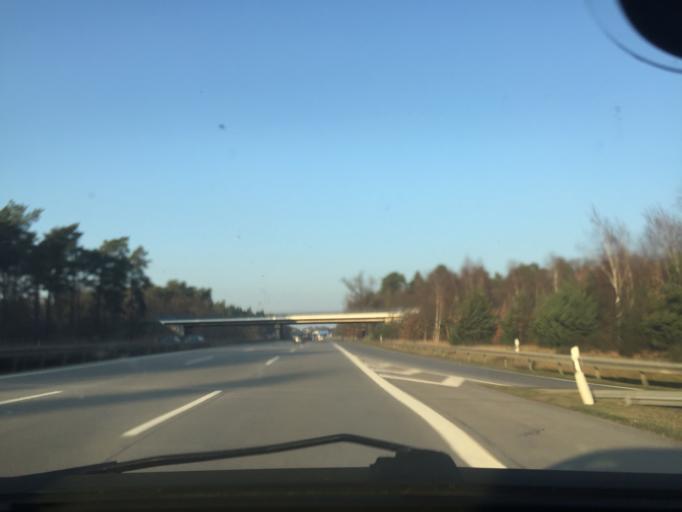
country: DE
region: Berlin
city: Wannsee
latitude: 52.3512
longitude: 13.1410
